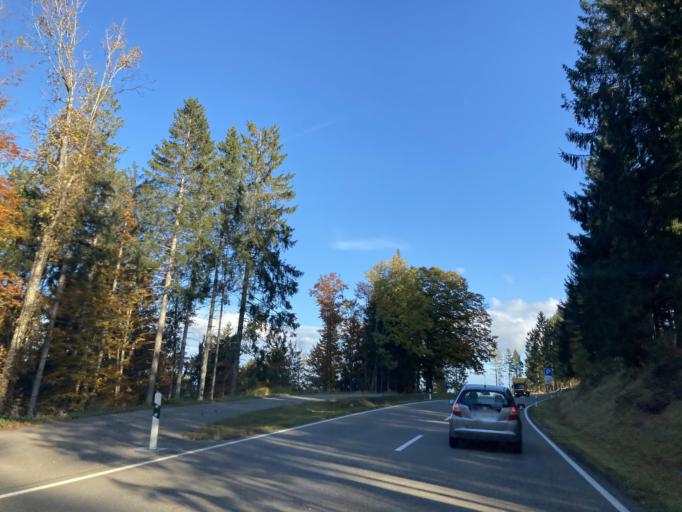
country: DE
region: Baden-Wuerttemberg
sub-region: Freiburg Region
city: Gutenbach
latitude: 47.9907
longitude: 8.1604
